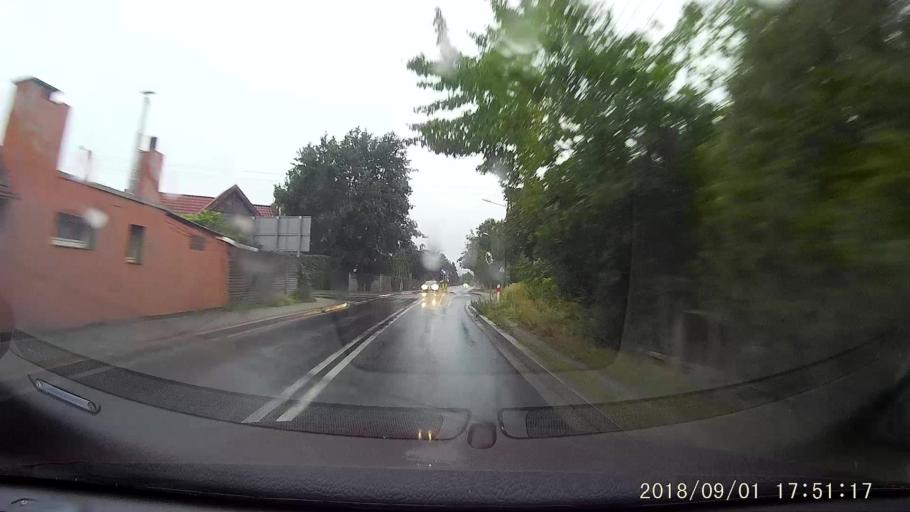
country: PL
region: Lubusz
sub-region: Powiat zaganski
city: Ilowa
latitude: 51.4985
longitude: 15.1928
